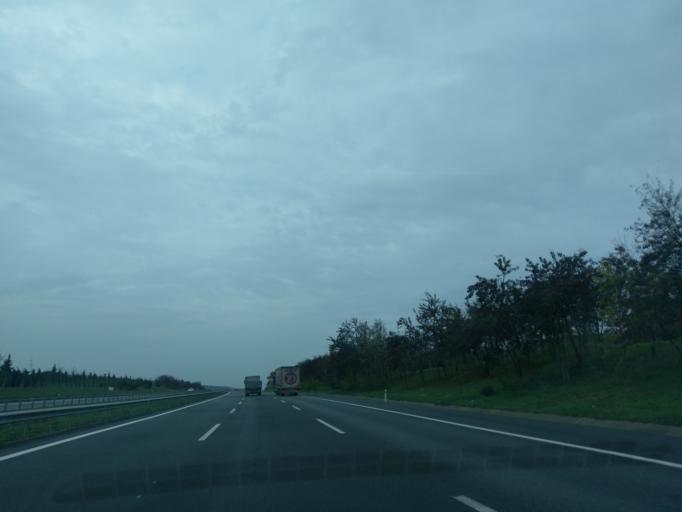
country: TR
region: Istanbul
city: Canta
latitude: 41.1627
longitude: 28.1331
